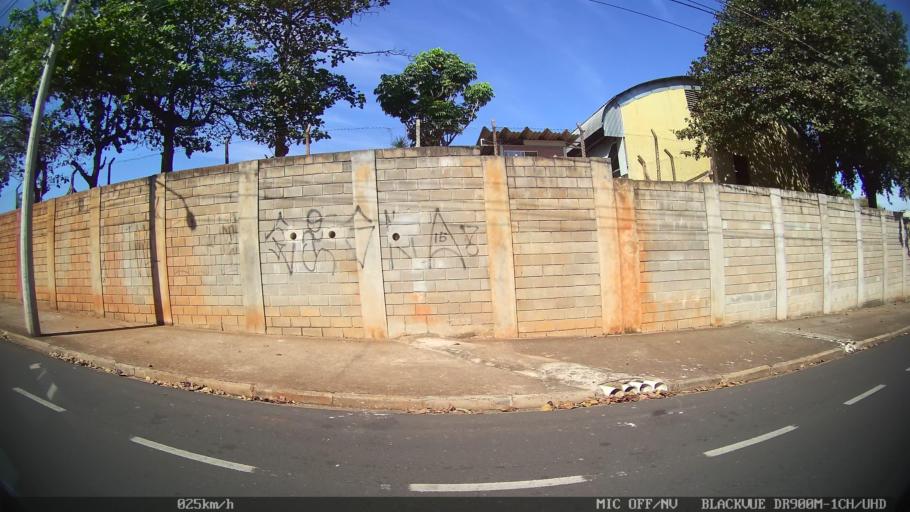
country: BR
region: Sao Paulo
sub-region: Sao Jose Do Rio Preto
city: Sao Jose do Rio Preto
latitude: -20.8107
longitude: -49.4132
